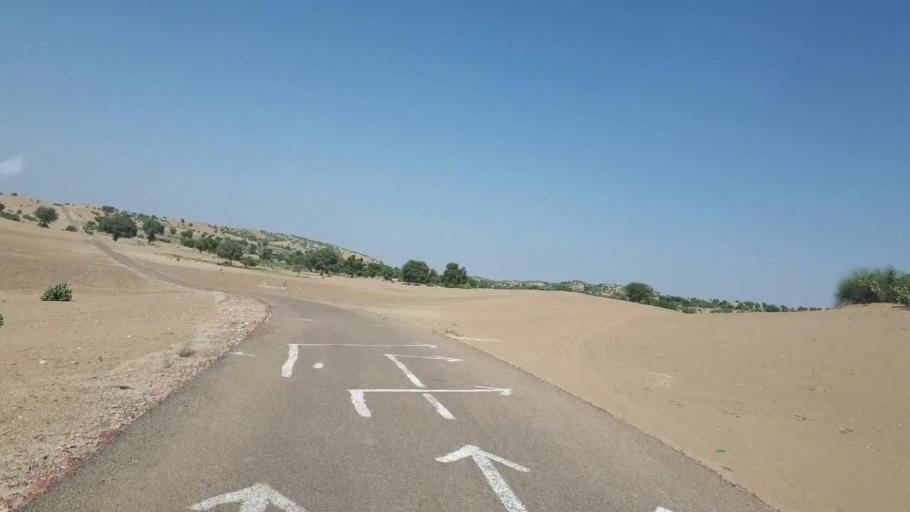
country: PK
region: Sindh
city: Chor
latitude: 25.6086
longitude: 70.3157
